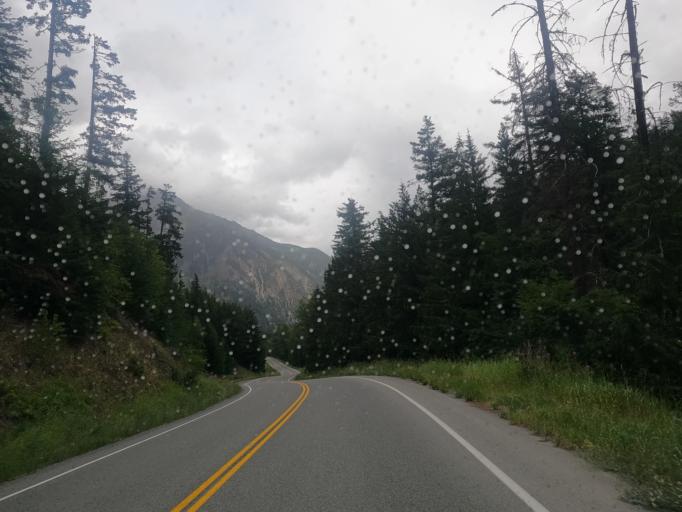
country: CA
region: British Columbia
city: Lillooet
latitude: 50.5175
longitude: -122.1687
